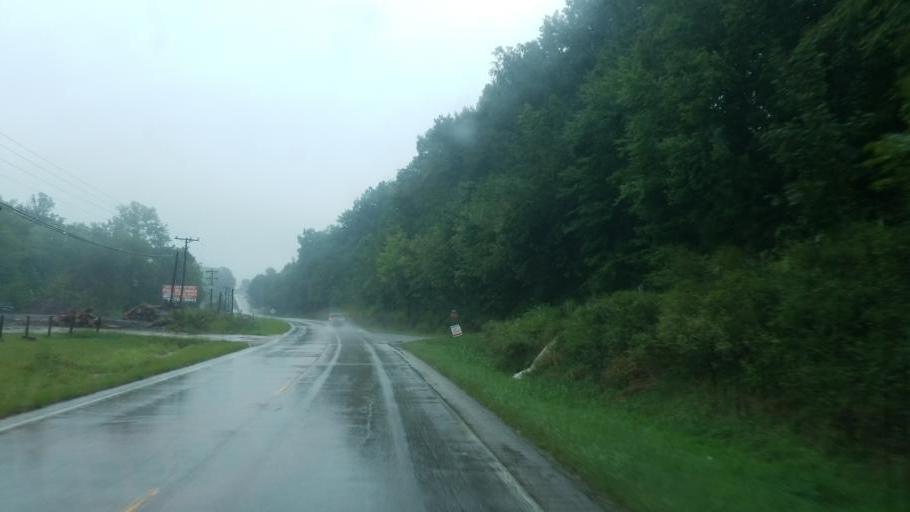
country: US
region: Kentucky
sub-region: Rowan County
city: Morehead
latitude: 38.2209
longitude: -83.4869
